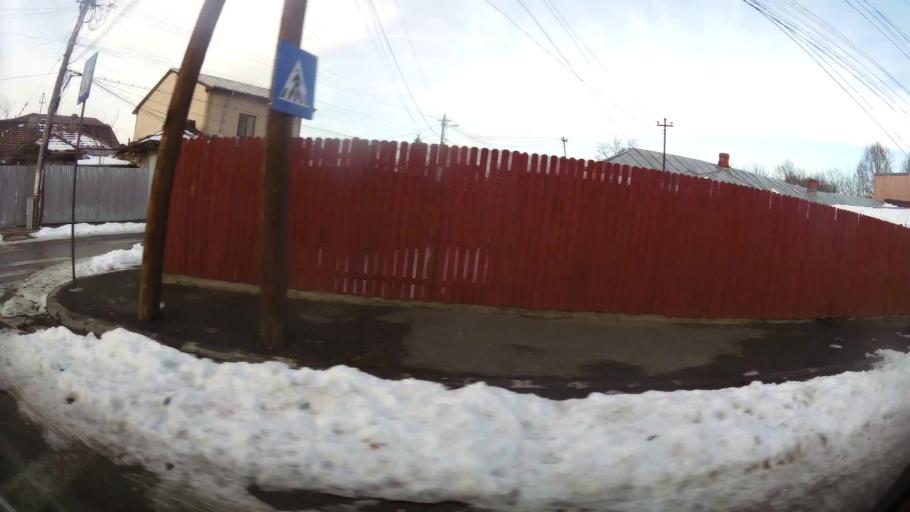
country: RO
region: Bucuresti
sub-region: Municipiul Bucuresti
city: Bucuresti
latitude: 44.3940
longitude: 26.0790
